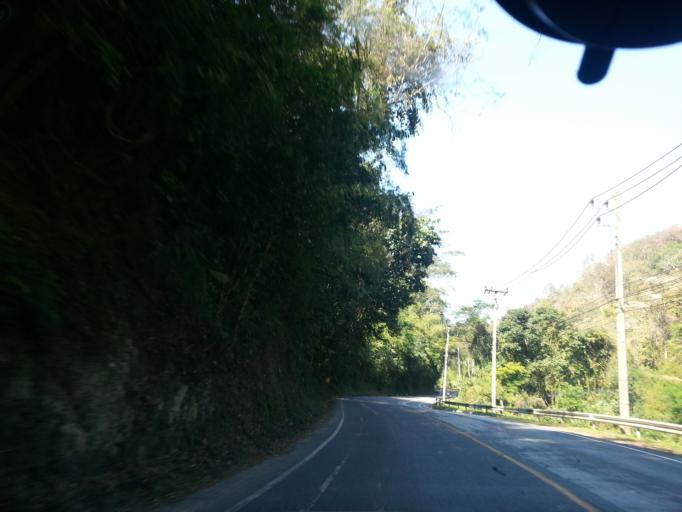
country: TH
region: Chiang Mai
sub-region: Amphoe Chiang Dao
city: Chiang Dao
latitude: 19.2761
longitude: 98.9711
